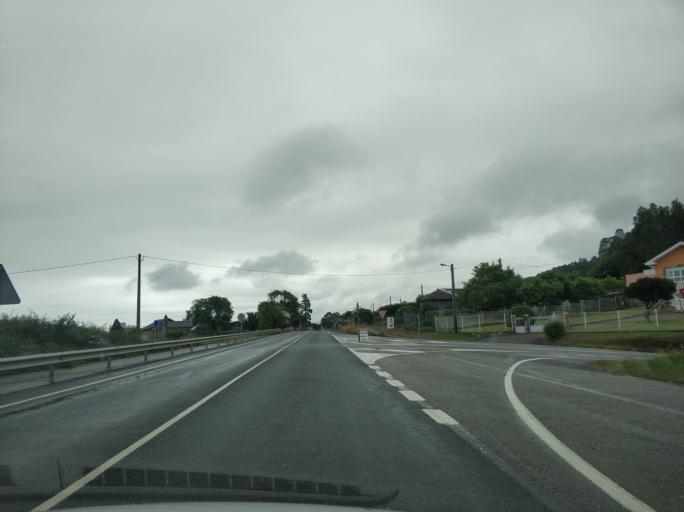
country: ES
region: Asturias
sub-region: Province of Asturias
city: Tineo
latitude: 43.5463
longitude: -6.4440
